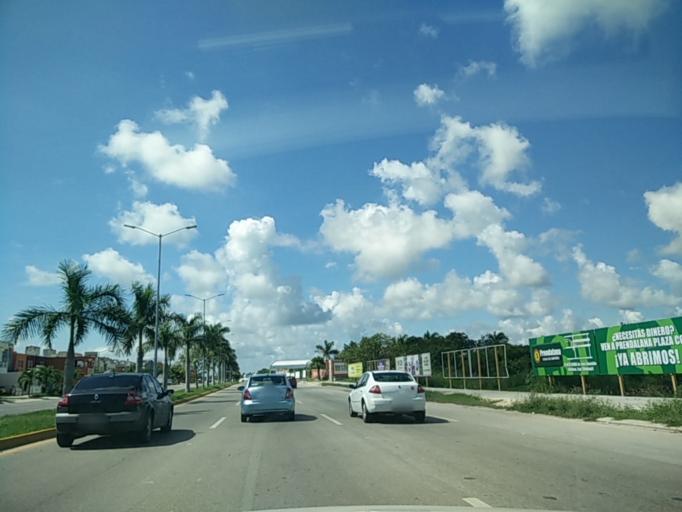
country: MX
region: Quintana Roo
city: Playa del Carmen
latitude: 20.6660
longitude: -87.0701
